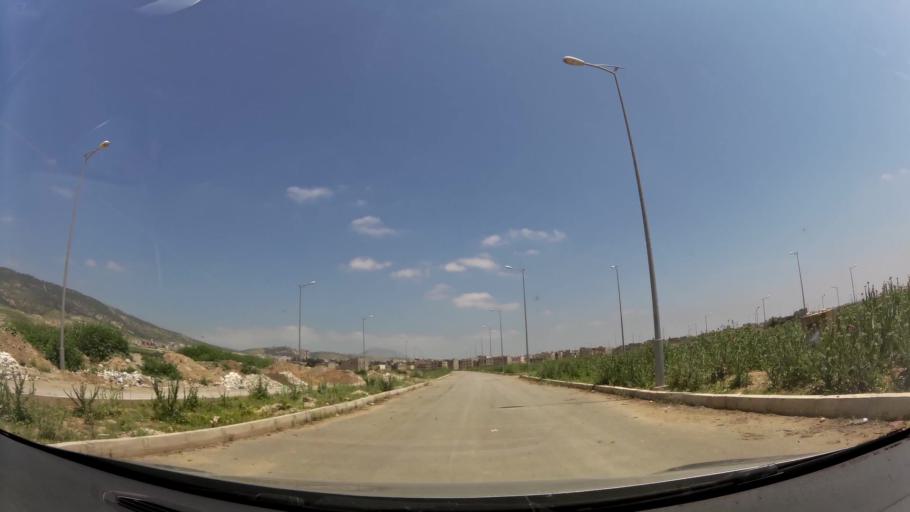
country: MA
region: Fes-Boulemane
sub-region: Fes
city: Fes
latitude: 34.0389
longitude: -5.0565
